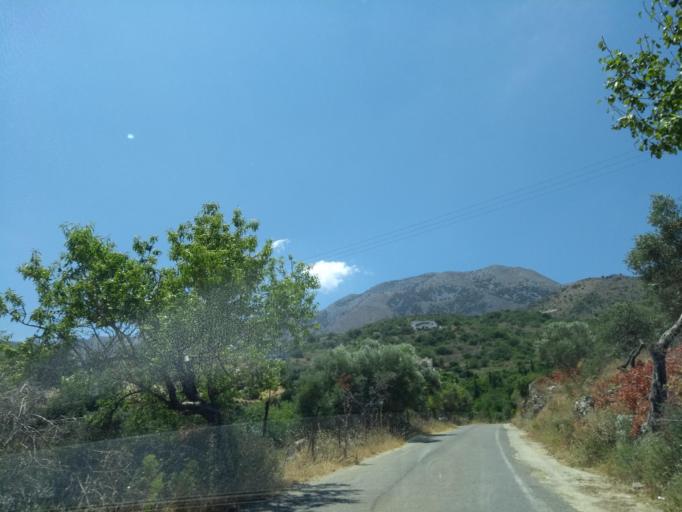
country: GR
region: Crete
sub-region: Nomos Chanias
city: Georgioupolis
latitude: 35.3194
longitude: 24.2896
